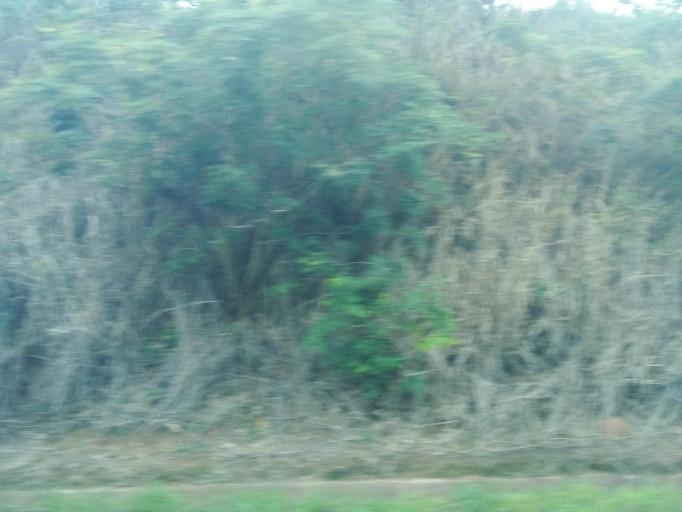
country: BR
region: Minas Gerais
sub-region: Governador Valadares
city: Governador Valadares
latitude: -19.0688
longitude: -42.1508
